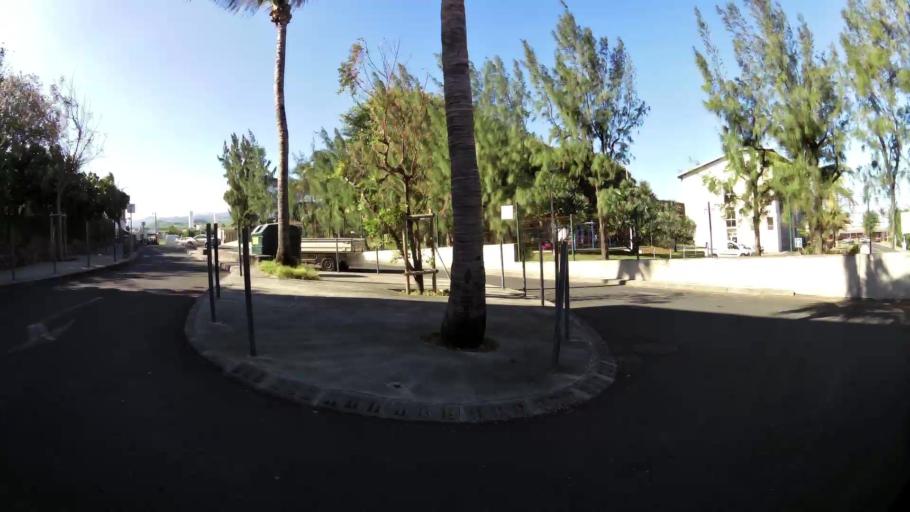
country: RE
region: Reunion
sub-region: Reunion
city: Saint-Pierre
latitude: -21.3482
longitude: 55.4902
